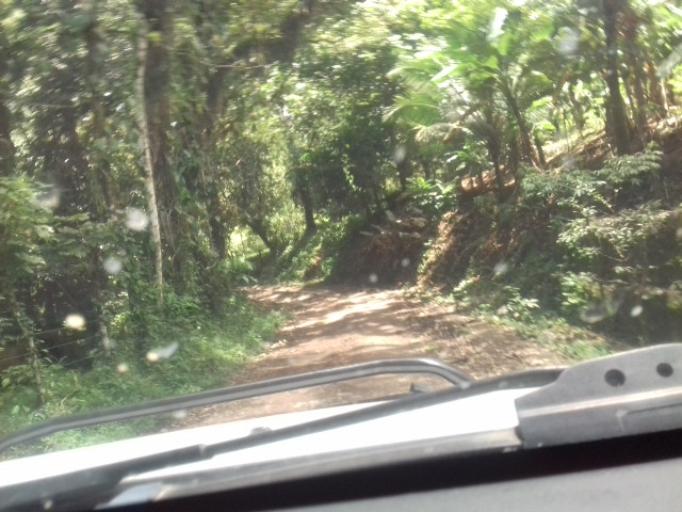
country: NI
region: Matagalpa
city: Rio Blanco
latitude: 12.9761
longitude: -85.3714
